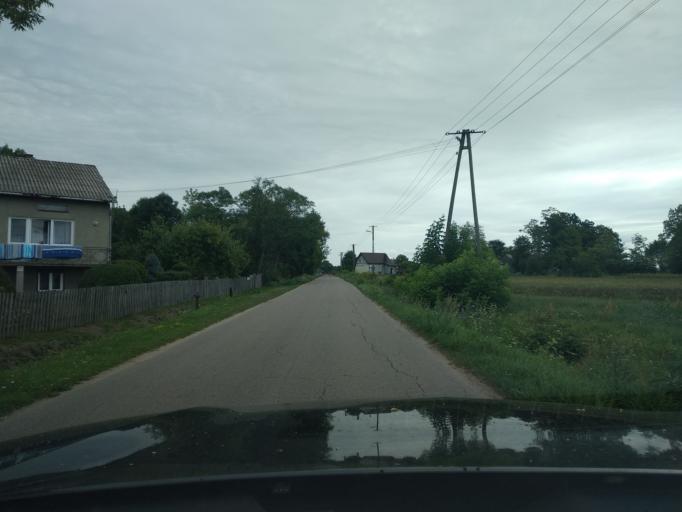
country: PL
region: Masovian Voivodeship
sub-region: Powiat pultuski
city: Obryte
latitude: 52.7533
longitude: 21.2064
